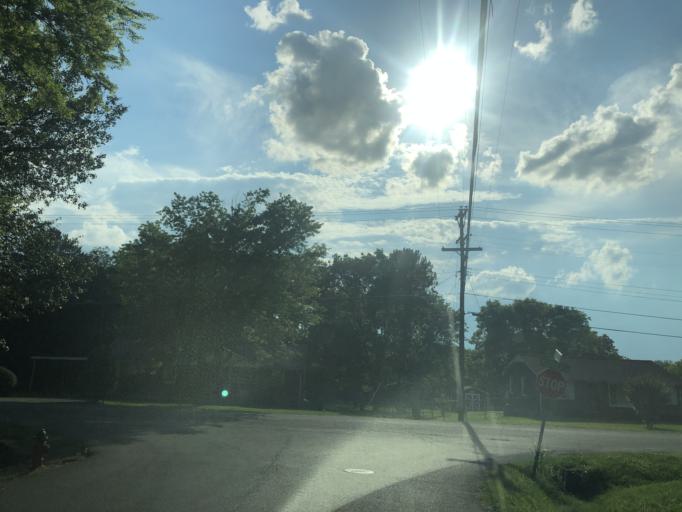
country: US
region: Tennessee
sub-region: Davidson County
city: Nashville
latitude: 36.2302
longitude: -86.7897
